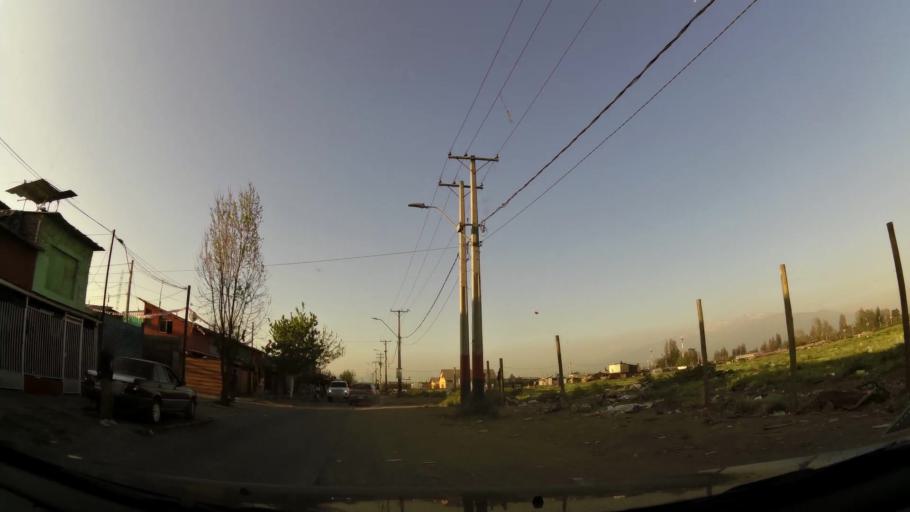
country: CL
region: Santiago Metropolitan
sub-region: Provincia de Maipo
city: San Bernardo
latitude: -33.5948
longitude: -70.6687
